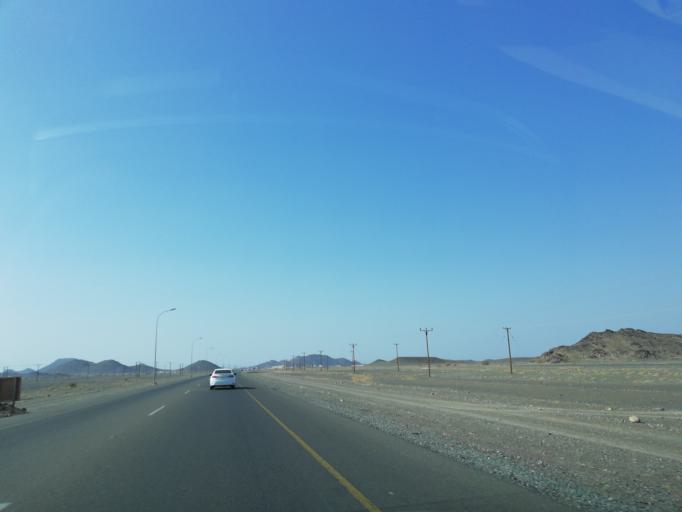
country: OM
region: Ash Sharqiyah
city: Ibra'
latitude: 22.7428
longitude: 58.1496
